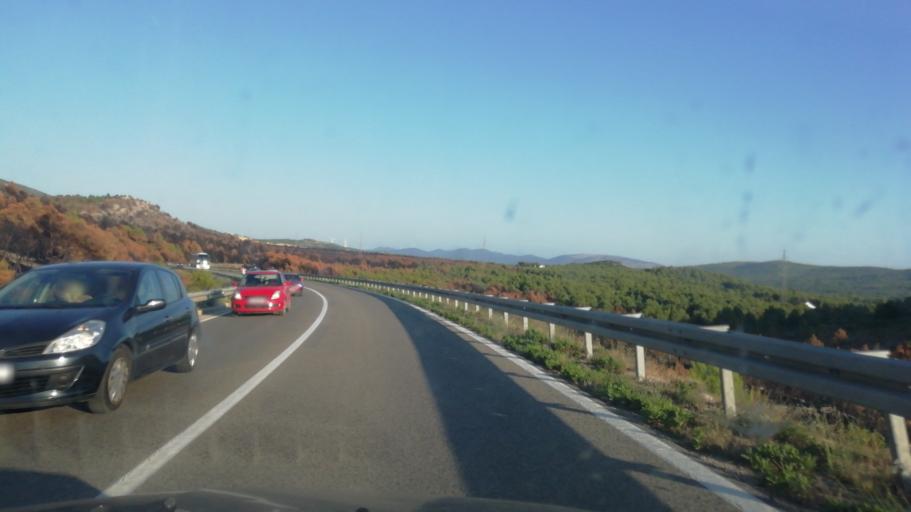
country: HR
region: Sibensko-Kniniska
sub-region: Grad Sibenik
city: Sibenik
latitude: 43.7514
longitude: 15.9373
